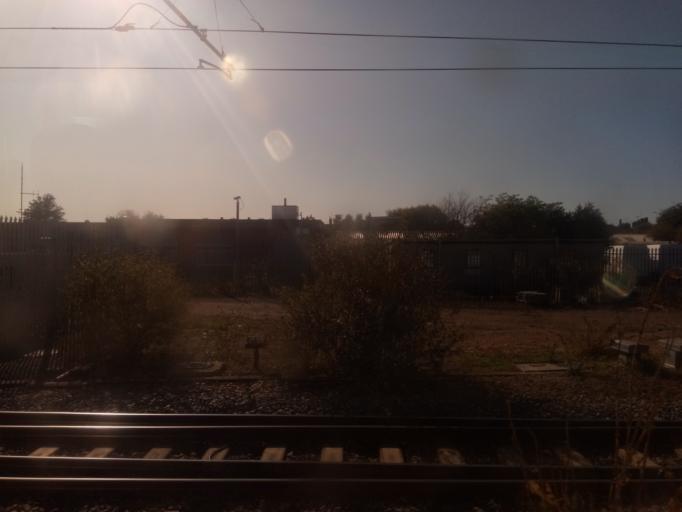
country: GB
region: England
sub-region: Peterborough
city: Peterborough
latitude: 52.5780
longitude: -0.2525
